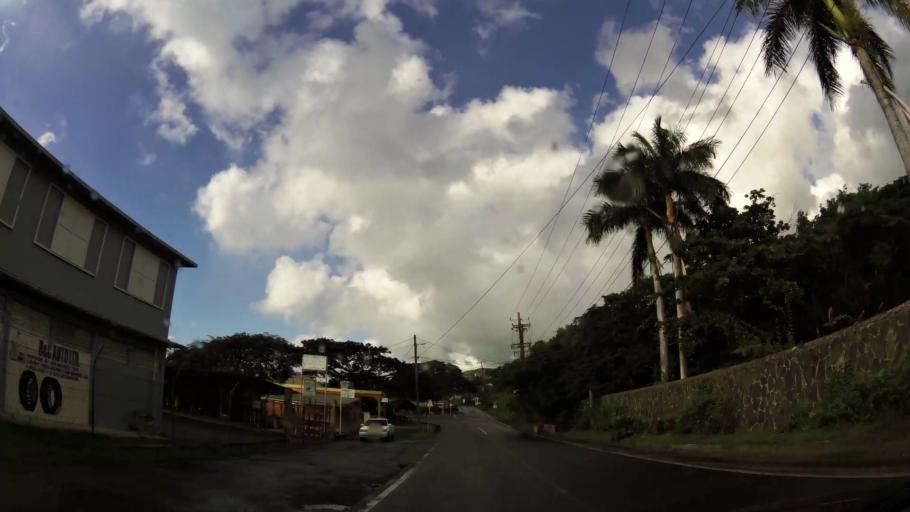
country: DM
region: Saint Paul
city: Mahaut
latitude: 15.3337
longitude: -61.3900
